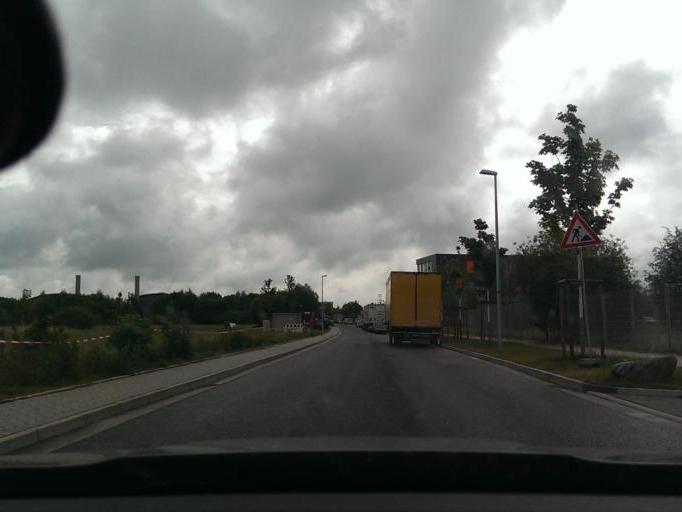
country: DE
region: Lower Saxony
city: Lehre
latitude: 52.3721
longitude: 10.7281
